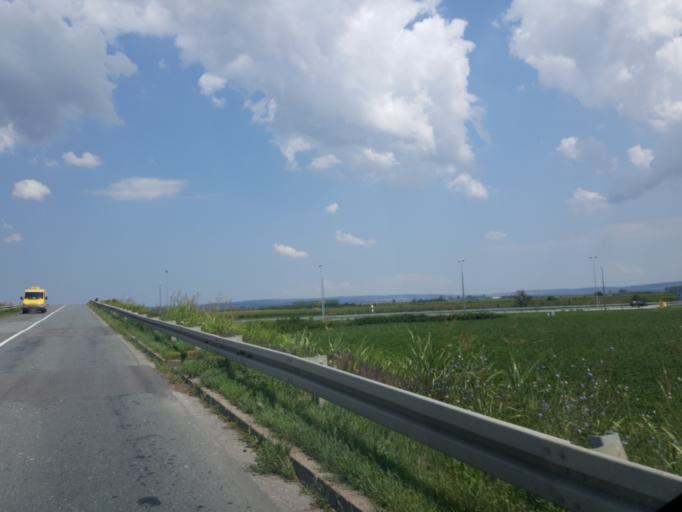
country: RS
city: Ravnje
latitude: 45.0382
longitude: 19.3828
